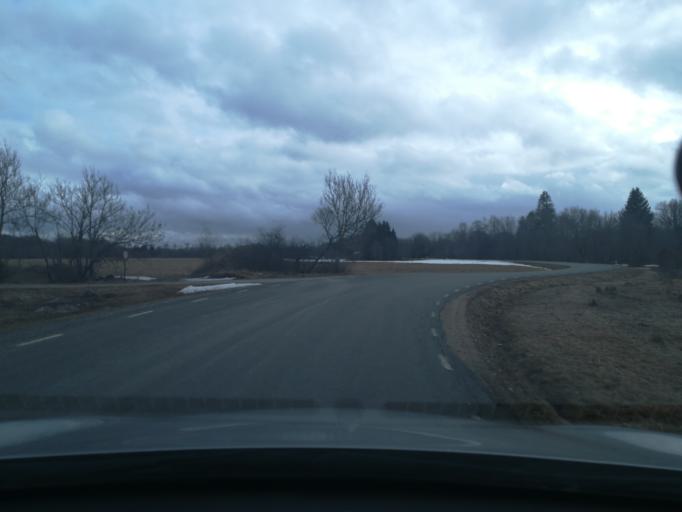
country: EE
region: Harju
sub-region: Saue linn
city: Saue
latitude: 59.3581
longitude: 24.5313
